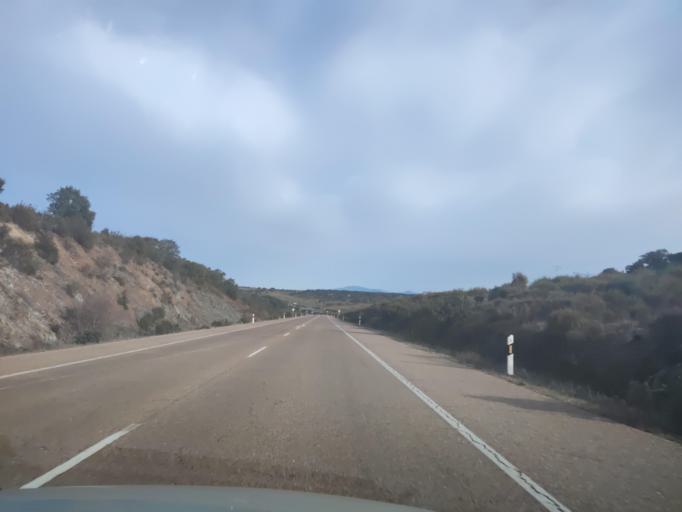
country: ES
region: Castille and Leon
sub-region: Provincia de Salamanca
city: Carpio de Azaba
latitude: 40.5909
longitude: -6.6779
